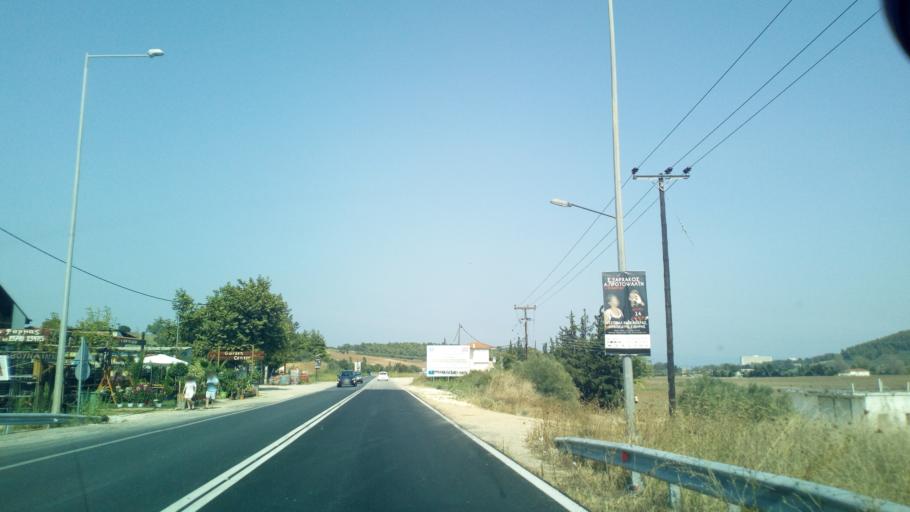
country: GR
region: Central Macedonia
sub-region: Nomos Chalkidikis
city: Kallithea
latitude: 40.0600
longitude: 23.4332
